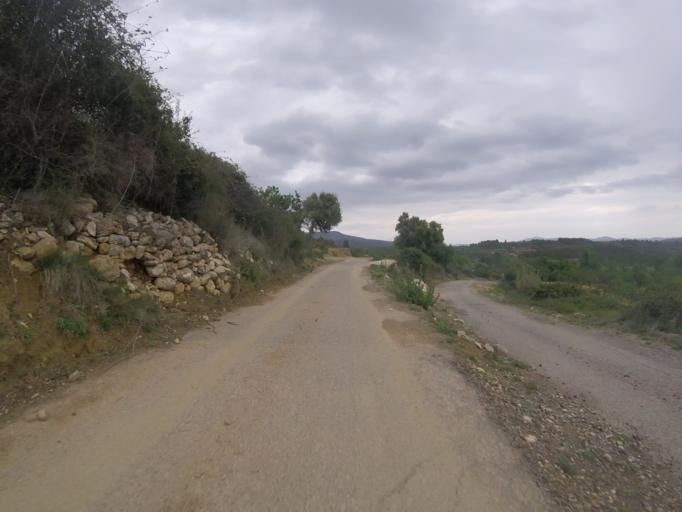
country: ES
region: Valencia
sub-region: Provincia de Castello
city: Sarratella
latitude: 40.2670
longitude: 0.0697
